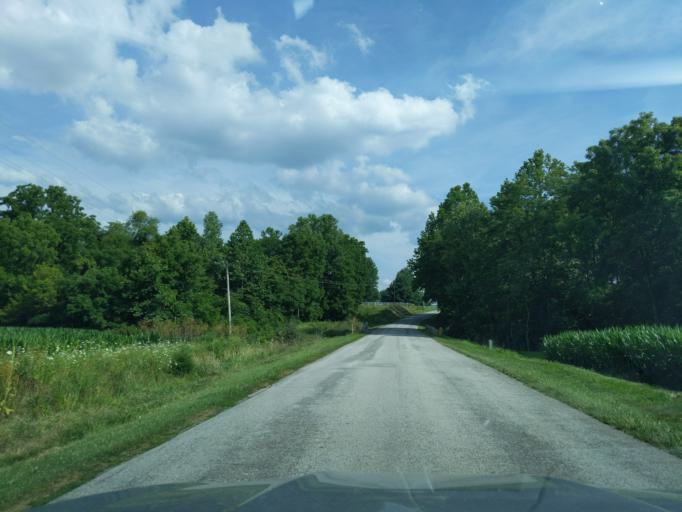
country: US
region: Indiana
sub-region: Decatur County
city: Greensburg
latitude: 39.2888
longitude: -85.4673
